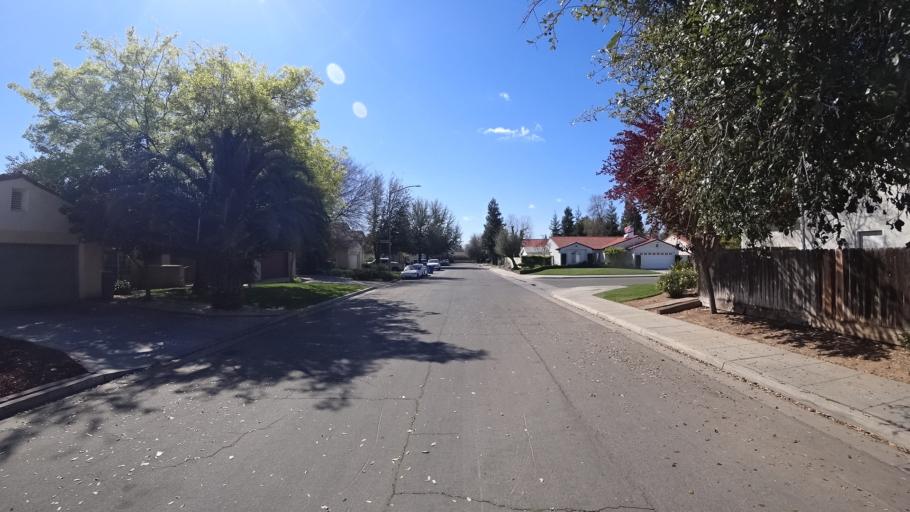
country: US
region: California
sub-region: Fresno County
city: West Park
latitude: 36.7885
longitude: -119.8866
